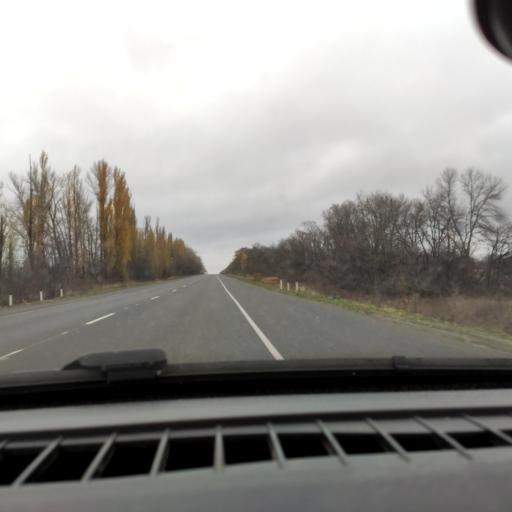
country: RU
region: Voronezj
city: Kolodeznyy
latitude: 51.2514
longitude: 39.0544
